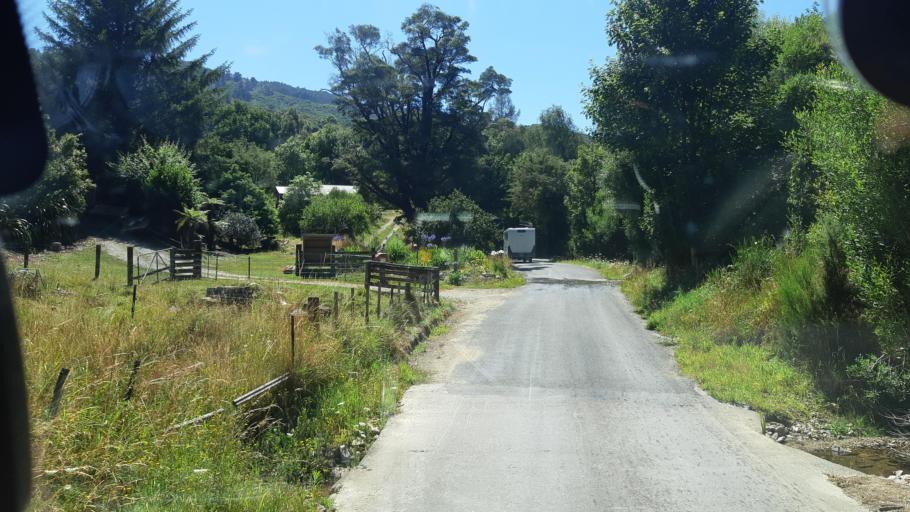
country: NZ
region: Tasman
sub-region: Tasman District
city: Motueka
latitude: -41.0361
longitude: 172.9050
